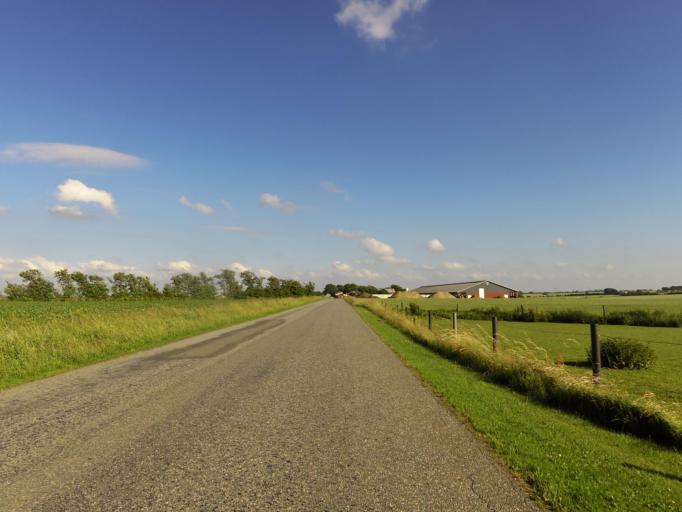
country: DK
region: South Denmark
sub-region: Vejen Kommune
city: Rodding
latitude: 55.3410
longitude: 9.1500
